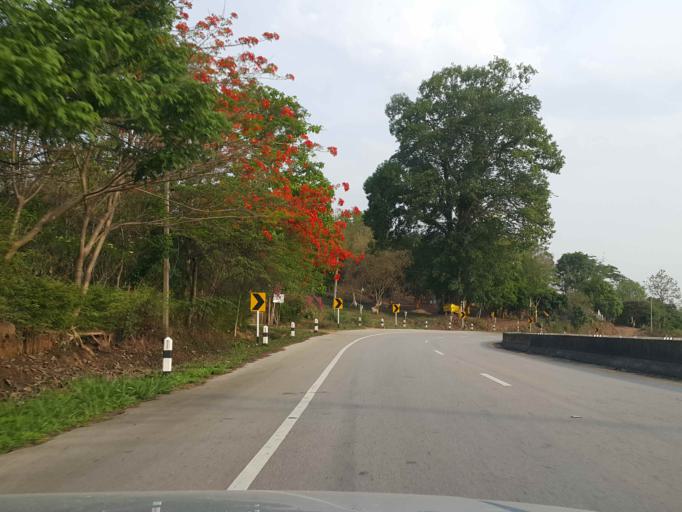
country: TH
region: Chiang Mai
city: Mae Taeng
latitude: 19.2376
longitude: 98.9682
